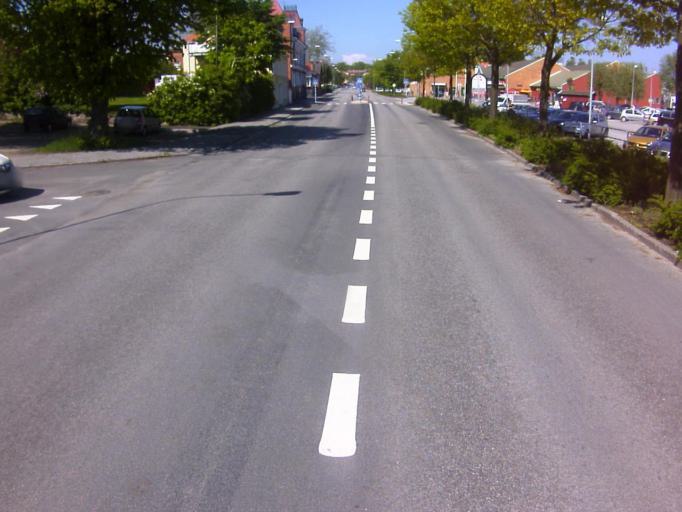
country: SE
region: Blekinge
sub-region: Solvesborgs Kommun
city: Soelvesborg
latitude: 56.0485
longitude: 14.5812
